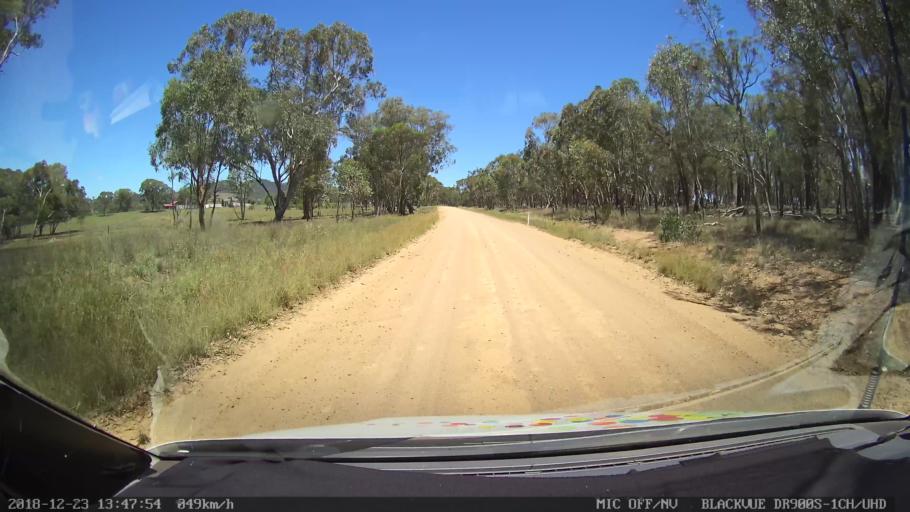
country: AU
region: New South Wales
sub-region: Tamworth Municipality
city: Manilla
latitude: -30.5134
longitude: 151.1154
